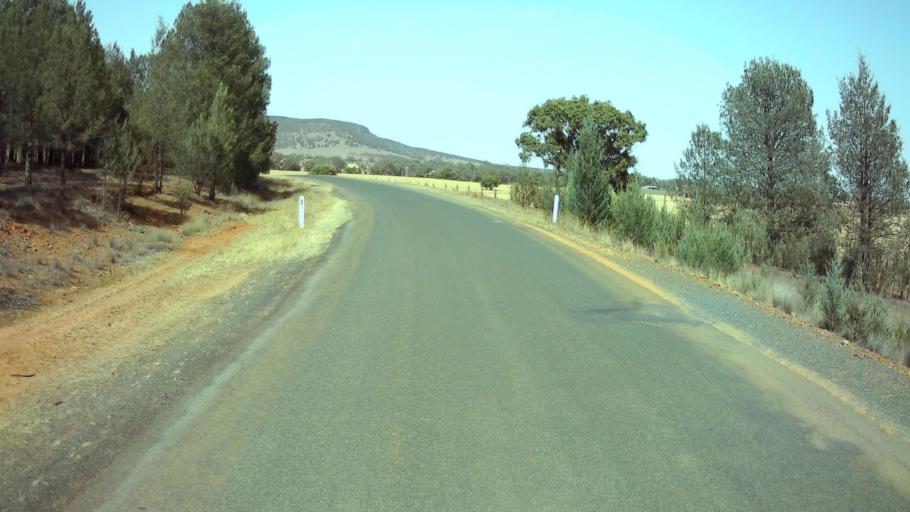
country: AU
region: New South Wales
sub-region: Weddin
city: Grenfell
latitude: -33.8616
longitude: 148.0144
